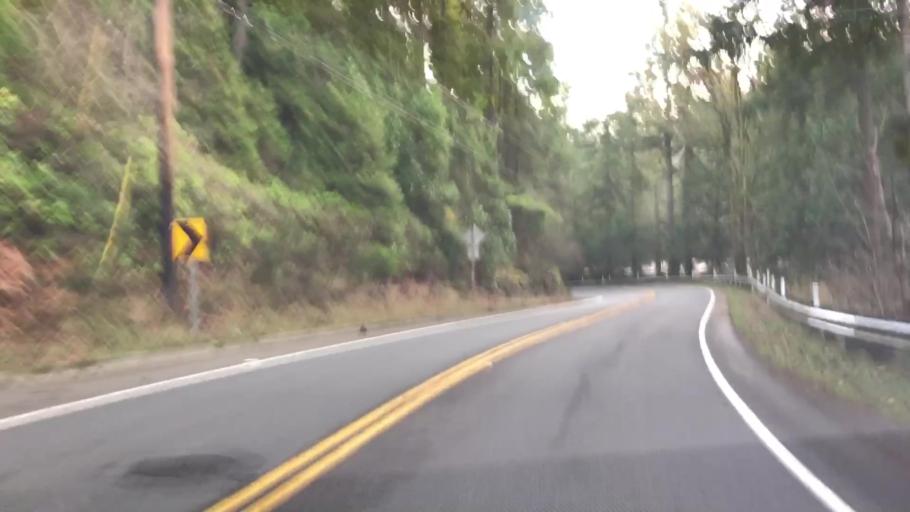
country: US
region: Washington
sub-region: King County
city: Eastgate
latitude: 47.5679
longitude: -122.1267
